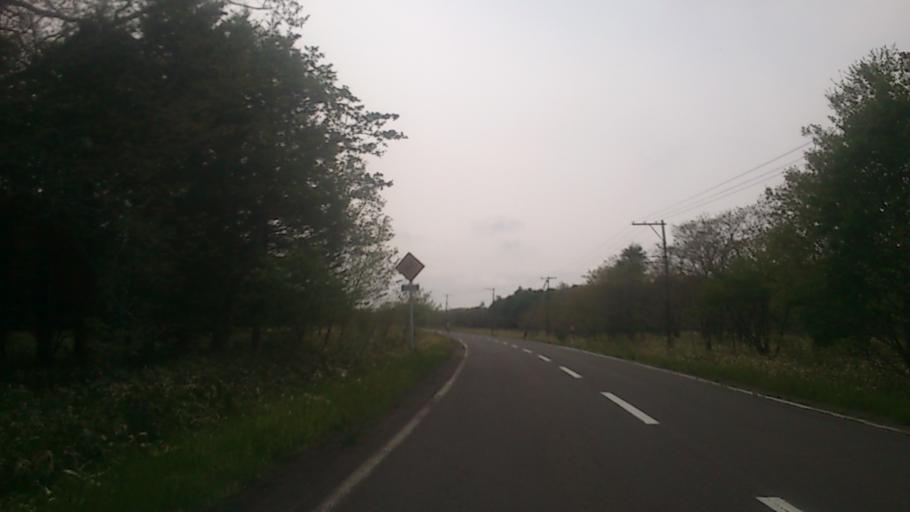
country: JP
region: Hokkaido
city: Nemuro
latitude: 43.2082
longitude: 145.3359
